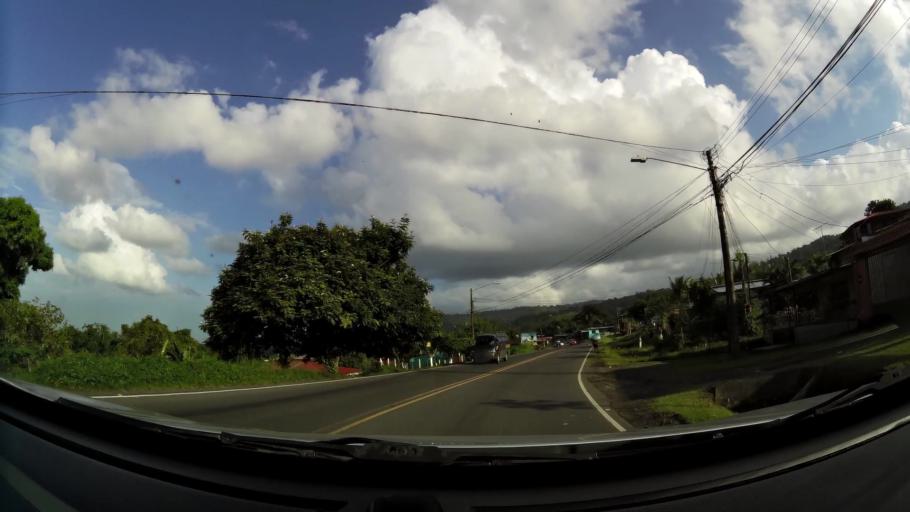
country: CR
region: Limon
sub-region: Canton de Siquirres
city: Siquirres
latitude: 10.0962
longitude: -83.5106
